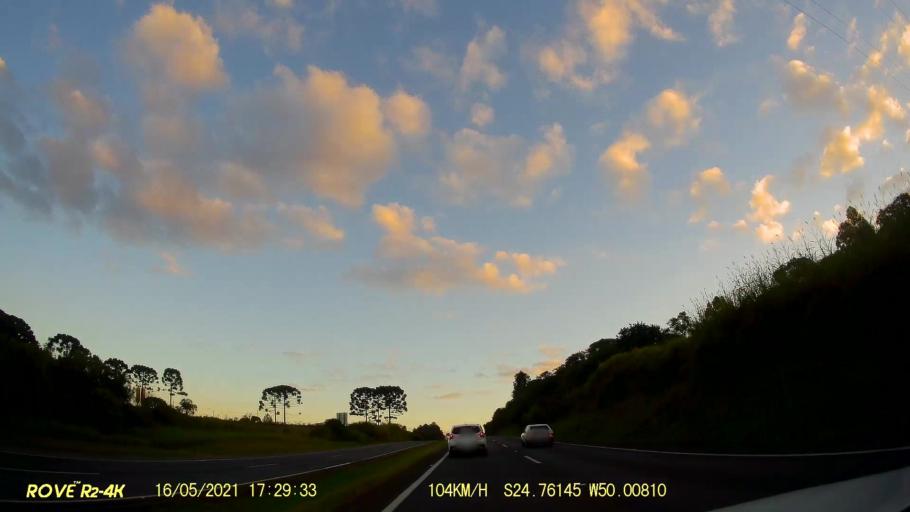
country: BR
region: Parana
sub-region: Castro
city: Castro
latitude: -24.7617
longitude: -50.0082
